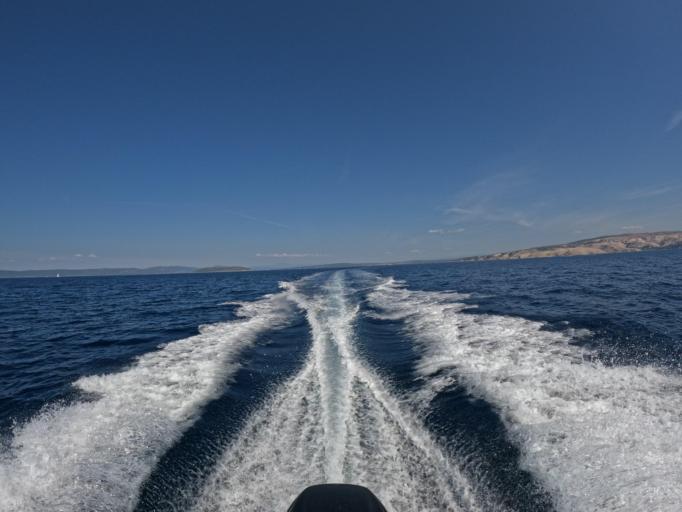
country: HR
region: Primorsko-Goranska
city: Punat
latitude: 44.9081
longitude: 14.6295
